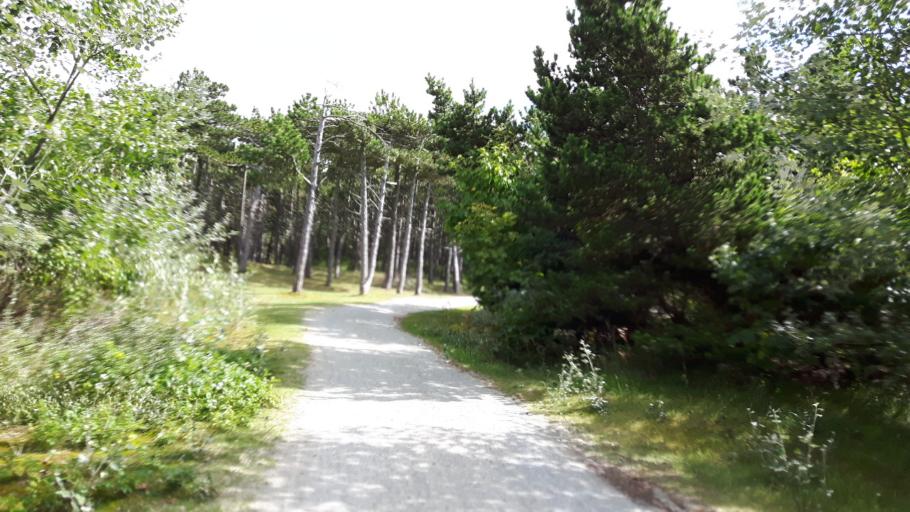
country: NL
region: Friesland
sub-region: Gemeente Ameland
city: Hollum
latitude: 53.4461
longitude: 5.6172
